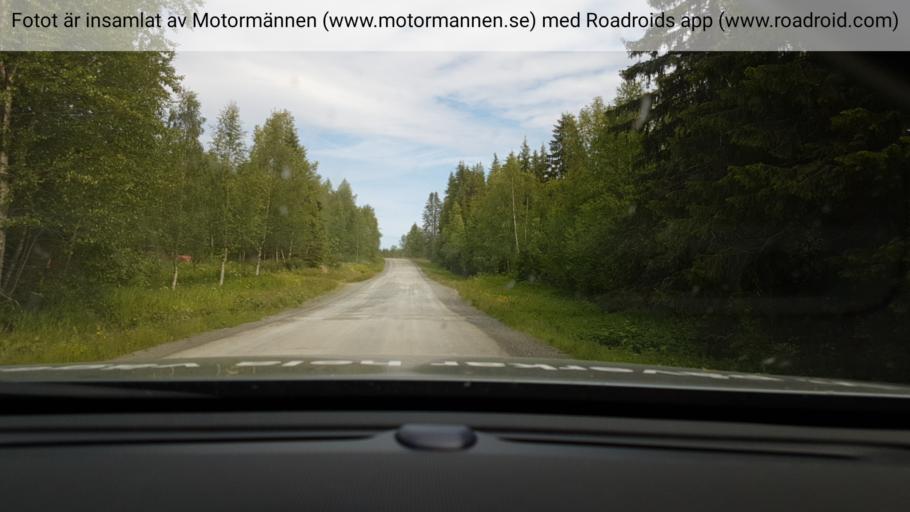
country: SE
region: Vaesterbotten
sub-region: Vilhelmina Kommun
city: Sjoberg
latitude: 65.1971
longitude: 16.1302
